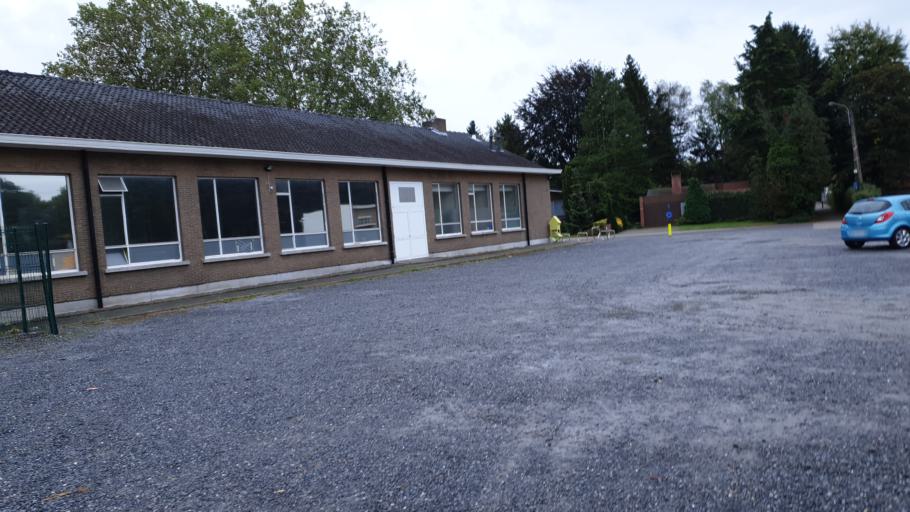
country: BE
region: Flanders
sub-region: Provincie Antwerpen
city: Westerlo
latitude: 51.0874
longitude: 4.9072
